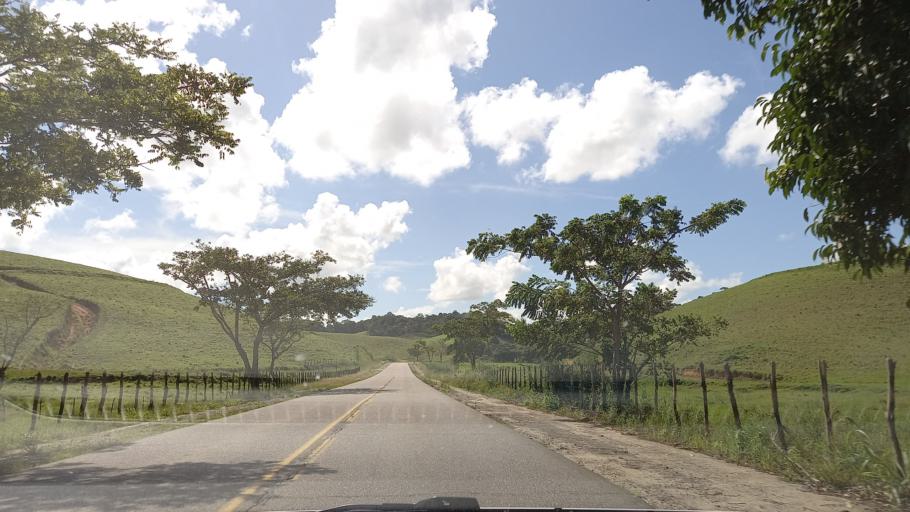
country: BR
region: Pernambuco
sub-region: Tamandare
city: Tamandare
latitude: -8.7451
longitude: -35.1721
